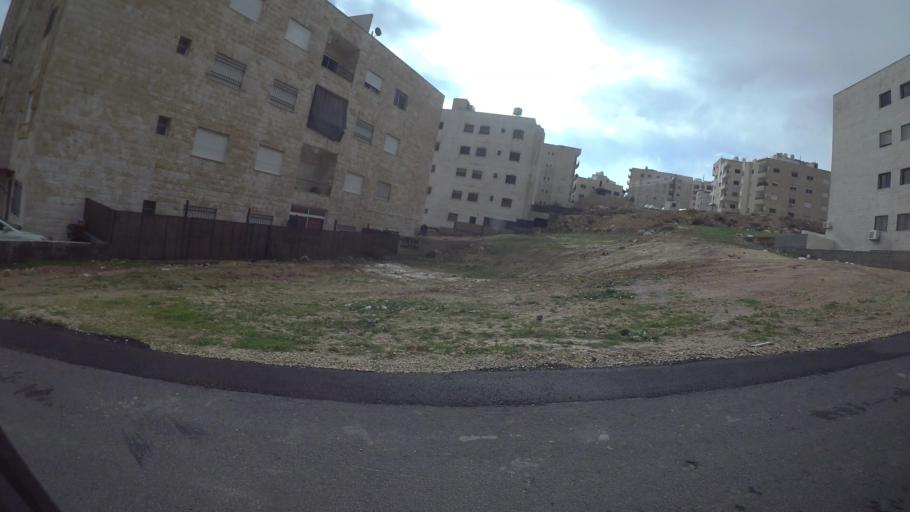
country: JO
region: Amman
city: Al Jubayhah
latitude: 32.0633
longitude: 35.8872
